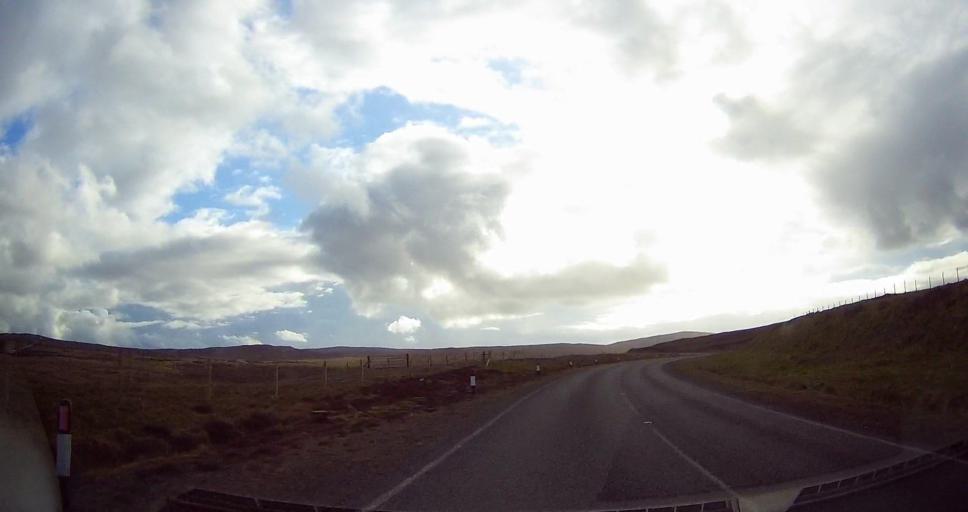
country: GB
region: Scotland
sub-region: Shetland Islands
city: Lerwick
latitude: 60.3493
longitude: -1.2098
